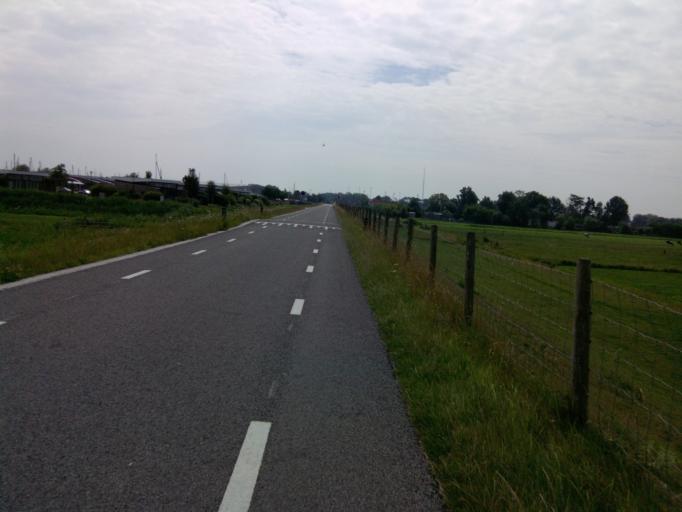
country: NL
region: Utrecht
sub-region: Gemeente Bunschoten
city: Spakenburg
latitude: 52.2624
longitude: 5.3677
